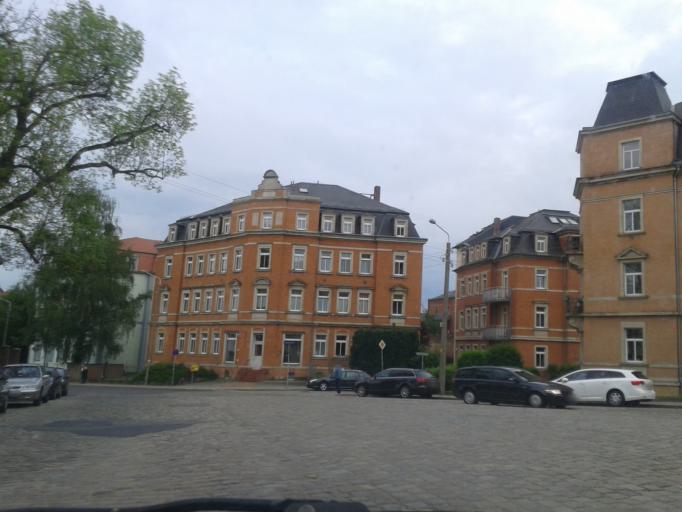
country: DE
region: Saxony
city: Dresden
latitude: 51.0323
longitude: 13.7002
